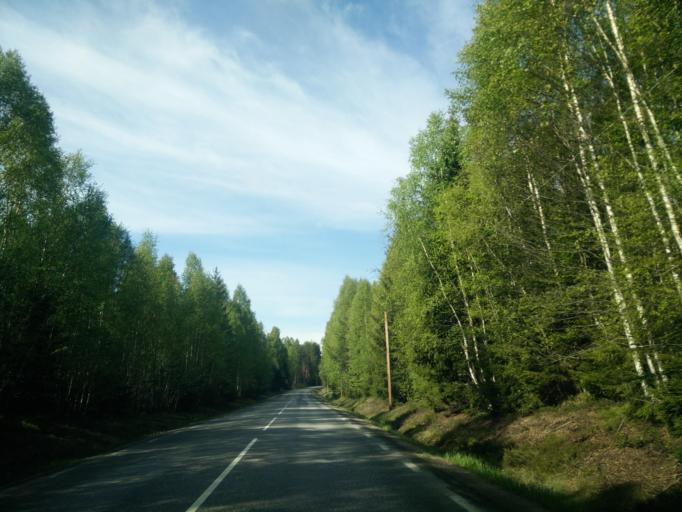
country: SE
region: Vaesternorrland
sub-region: Sundsvalls Kommun
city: Sundsvall
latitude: 62.3040
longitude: 17.2683
